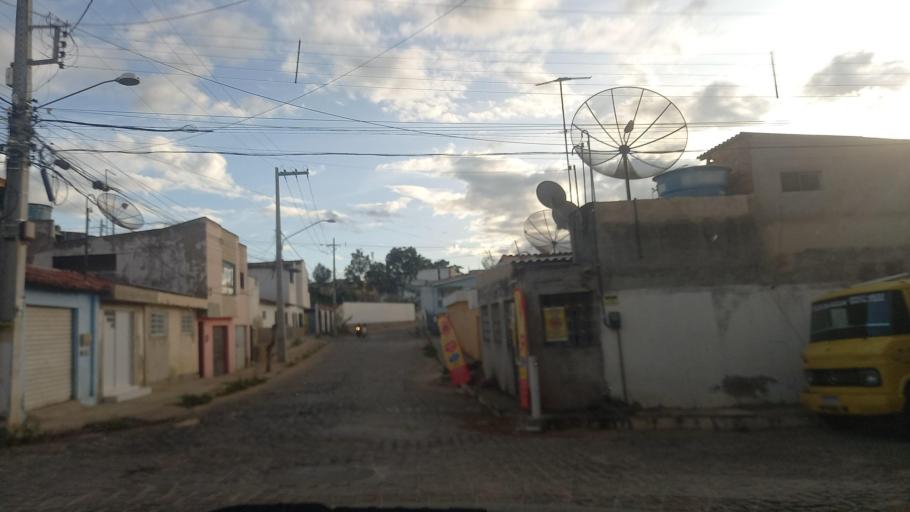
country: BR
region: Pernambuco
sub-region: Bezerros
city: Bezerros
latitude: -8.2373
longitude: -35.7500
